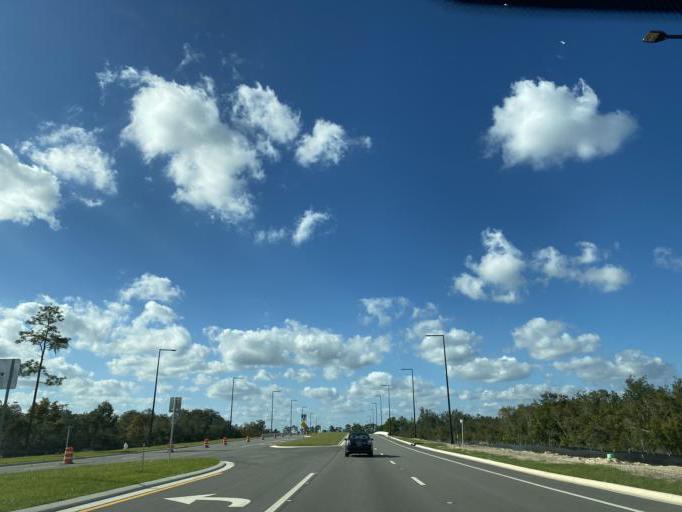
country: US
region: Florida
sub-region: Polk County
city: Citrus Ridge
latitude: 28.3809
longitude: -81.6289
